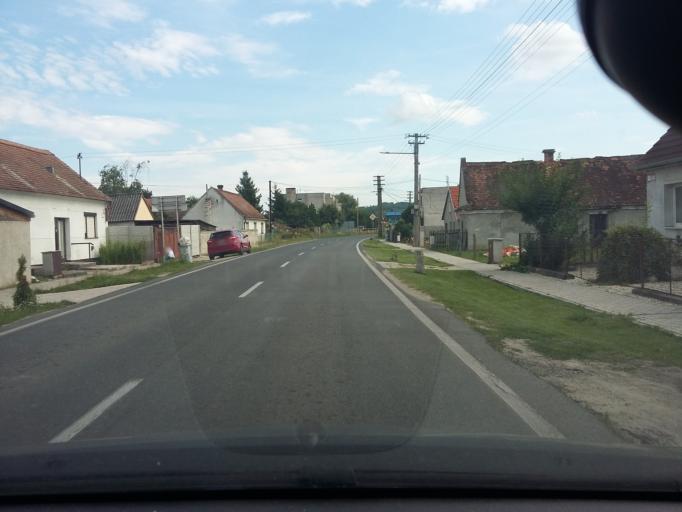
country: SK
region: Trnavsky
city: Gbely
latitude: 48.6268
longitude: 17.2048
